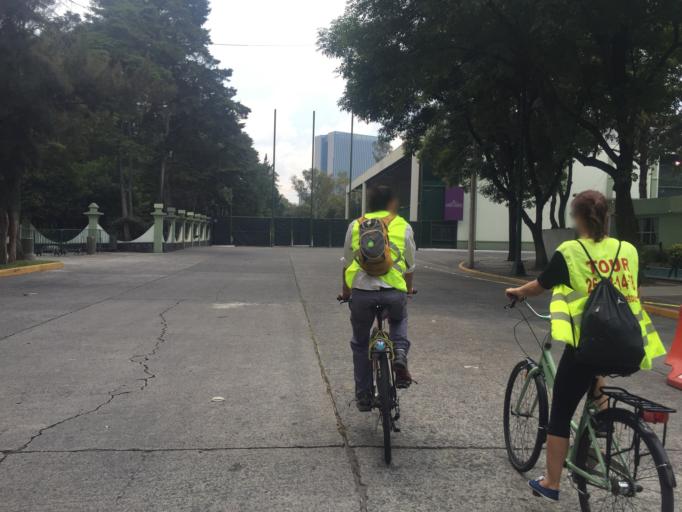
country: MX
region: Mexico City
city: Polanco
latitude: 19.4229
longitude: -99.1955
